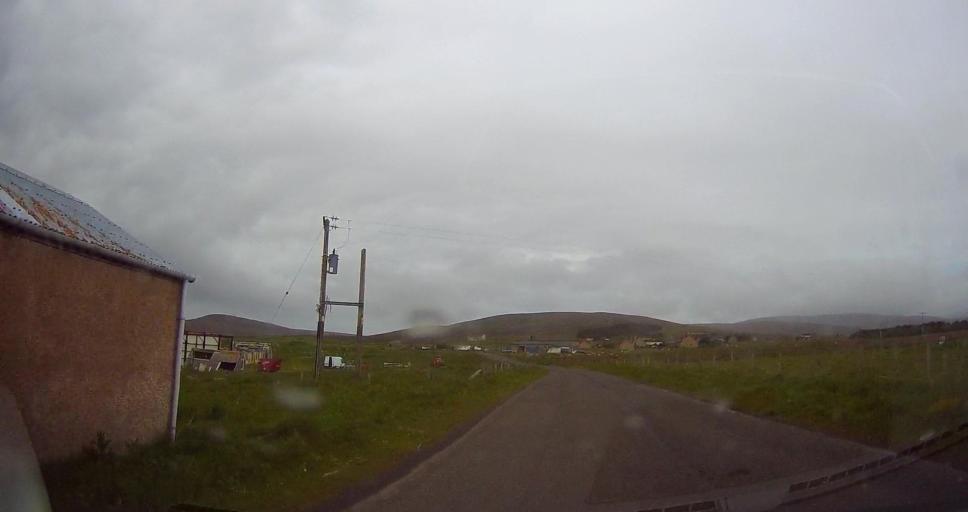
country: GB
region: Scotland
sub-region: Orkney Islands
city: Stromness
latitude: 58.8315
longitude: -3.1984
